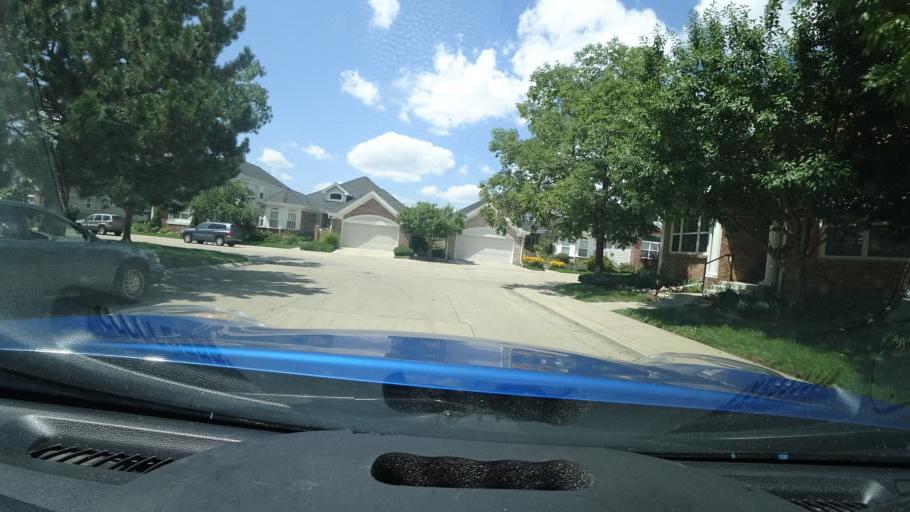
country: US
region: Colorado
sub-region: Arapahoe County
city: Glendale
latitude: 39.6995
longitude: -104.8974
